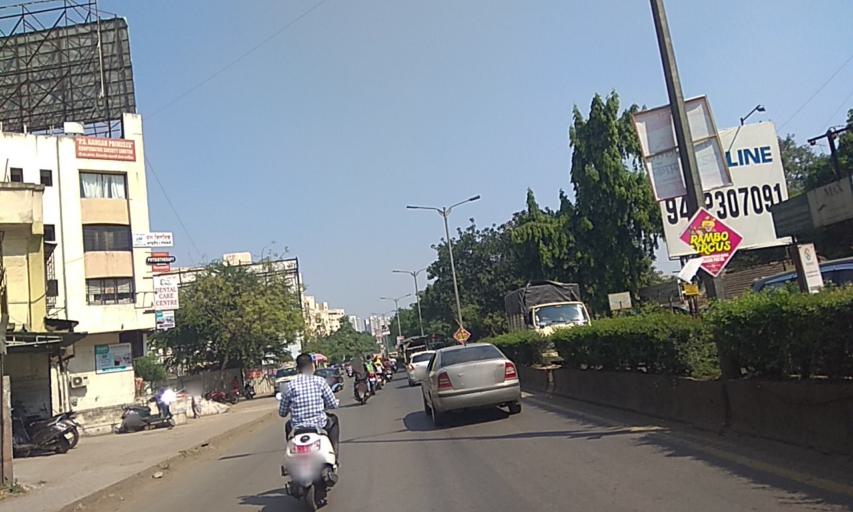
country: IN
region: Maharashtra
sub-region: Pune Division
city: Pune
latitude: 18.5074
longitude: 73.9289
